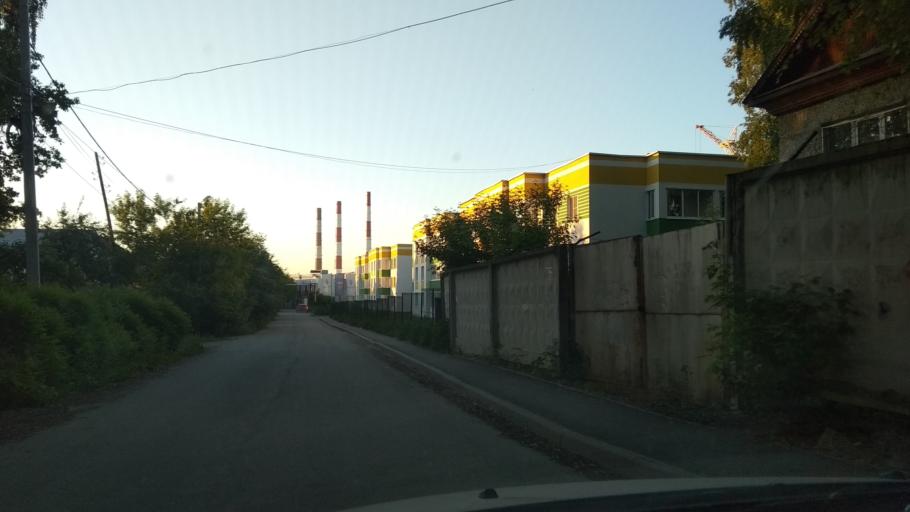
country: RU
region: Sverdlovsk
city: Sredneuralsk
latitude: 56.9900
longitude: 60.4574
